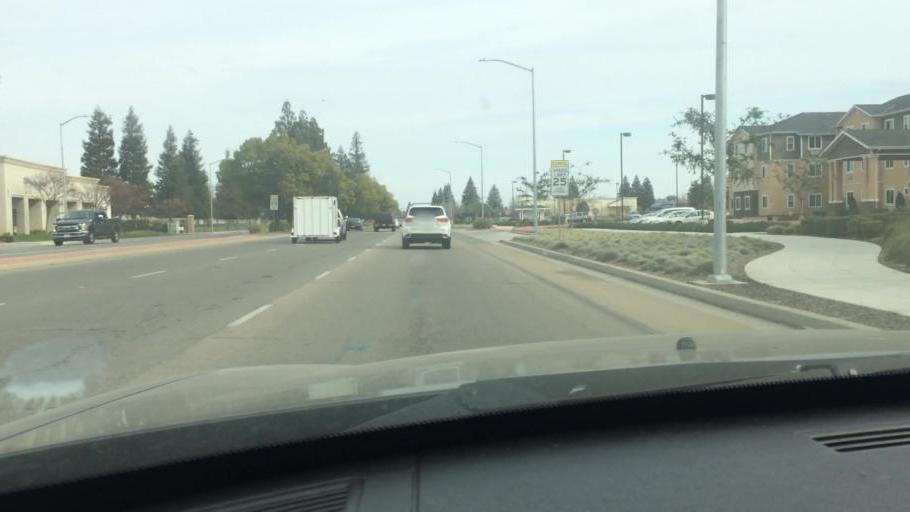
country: US
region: California
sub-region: Fresno County
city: Tarpey Village
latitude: 36.8085
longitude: -119.6864
